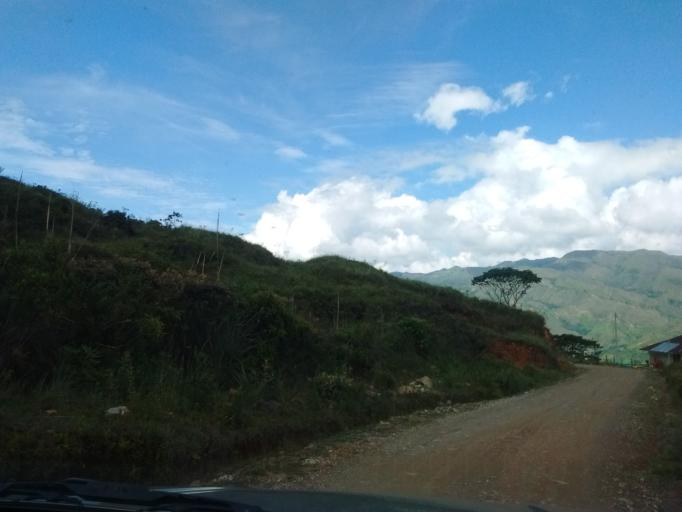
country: CO
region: Cauca
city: Morales
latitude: 2.6927
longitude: -76.7442
